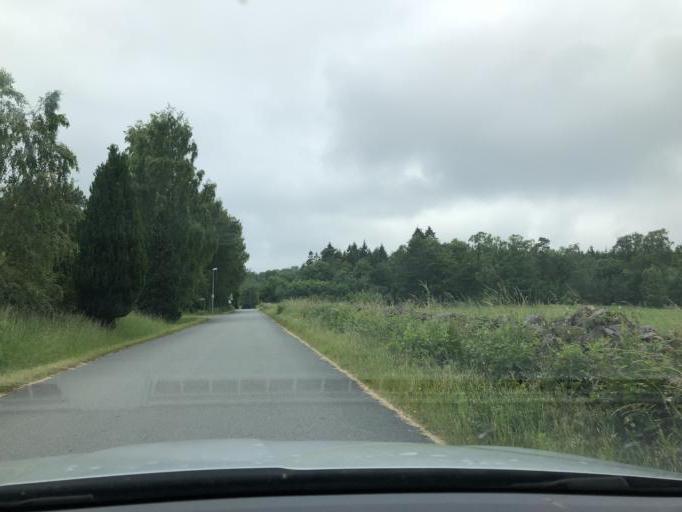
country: SE
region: Blekinge
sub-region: Solvesborgs Kommun
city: Soelvesborg
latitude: 56.1428
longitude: 14.5996
